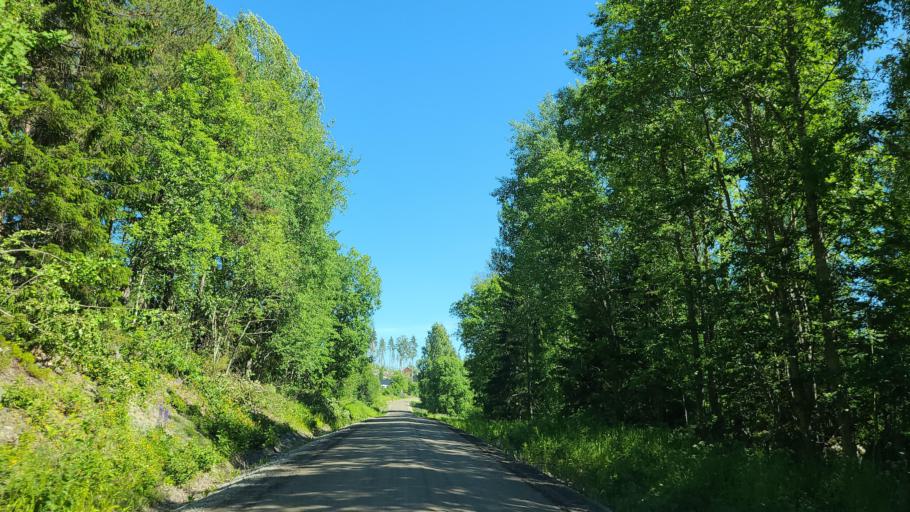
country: SE
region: Vaesterbotten
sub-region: Bjurholms Kommun
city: Bjurholm
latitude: 63.6758
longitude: 19.0180
